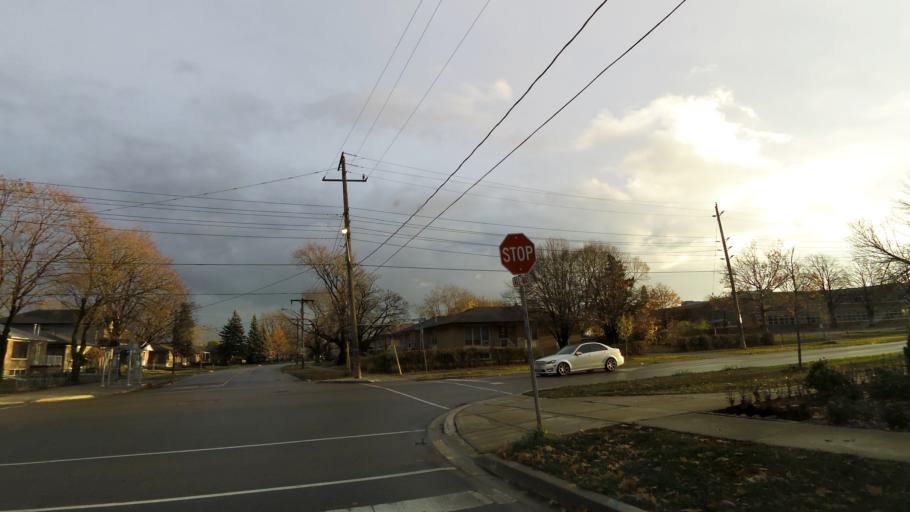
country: CA
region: Ontario
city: Etobicoke
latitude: 43.6609
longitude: -79.5810
